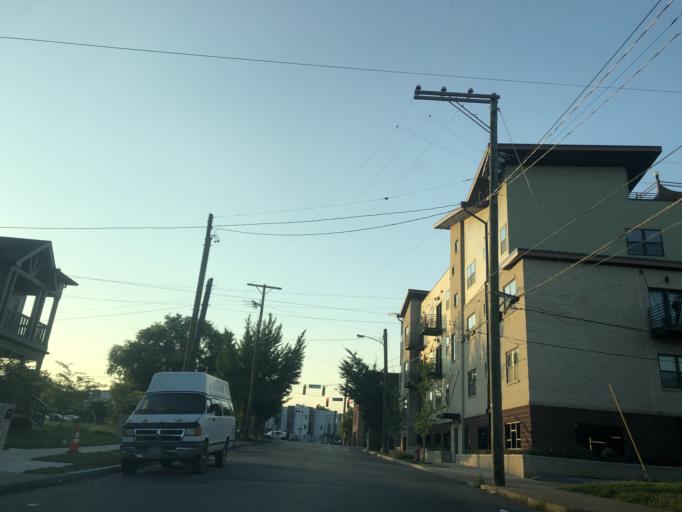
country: US
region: Tennessee
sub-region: Davidson County
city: Nashville
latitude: 36.1718
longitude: -86.7944
